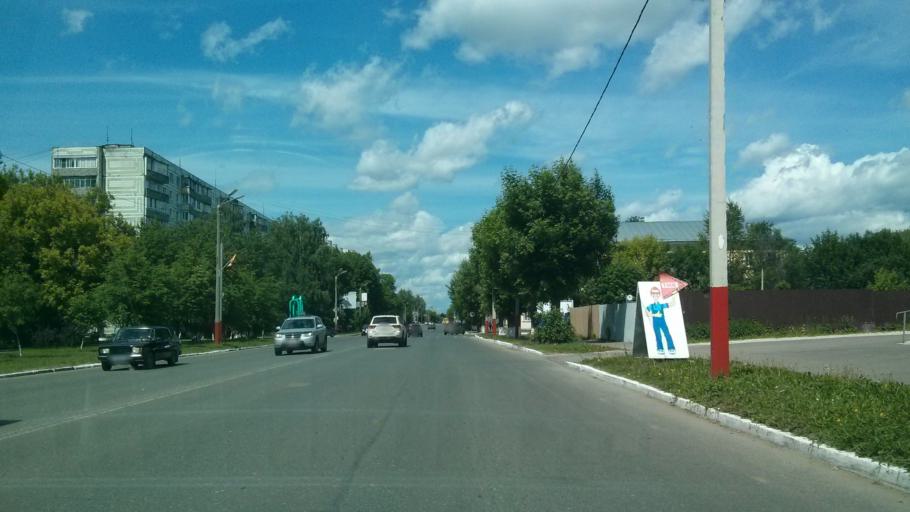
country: RU
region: Vladimir
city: Murom
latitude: 55.5697
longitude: 42.0594
